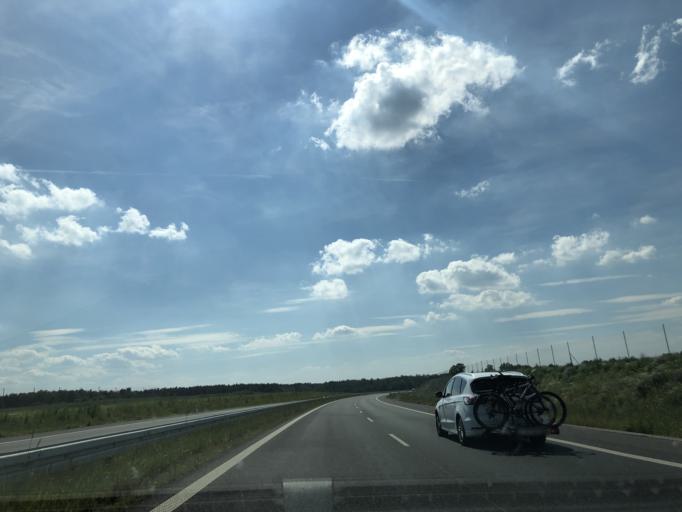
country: PL
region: West Pomeranian Voivodeship
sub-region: Powiat goleniowski
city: Osina
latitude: 53.6427
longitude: 15.0619
